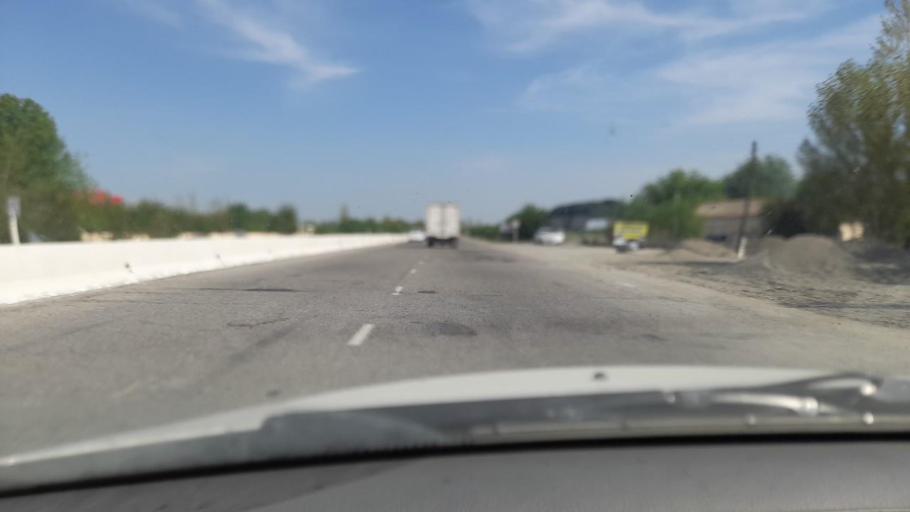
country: UZ
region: Samarqand
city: Chelak
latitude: 39.8500
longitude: 66.8025
